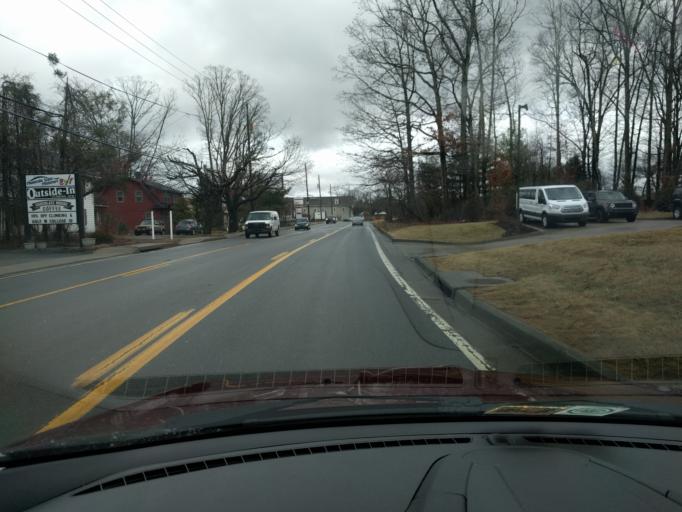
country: US
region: West Virginia
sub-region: Raleigh County
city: Mabscott
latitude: 37.7902
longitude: -81.2078
